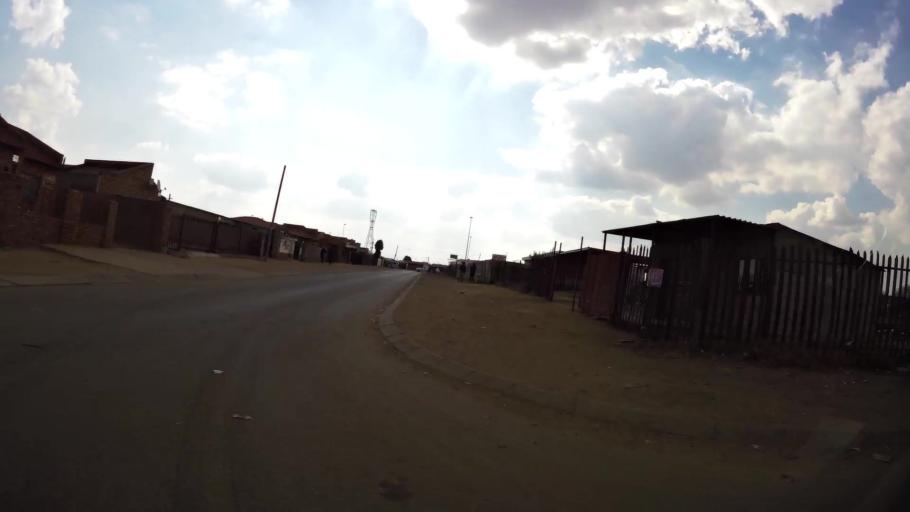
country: ZA
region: Gauteng
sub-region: Ekurhuleni Metropolitan Municipality
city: Springs
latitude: -26.1193
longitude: 28.4725
